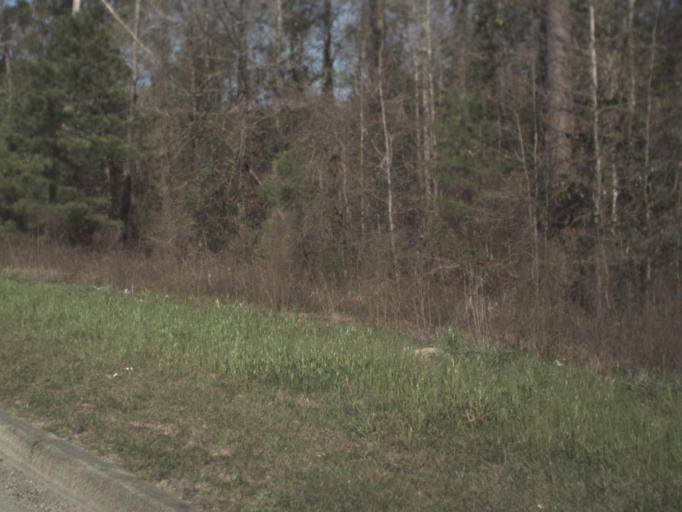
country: US
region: Florida
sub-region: Jackson County
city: Marianna
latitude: 30.7310
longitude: -85.1853
